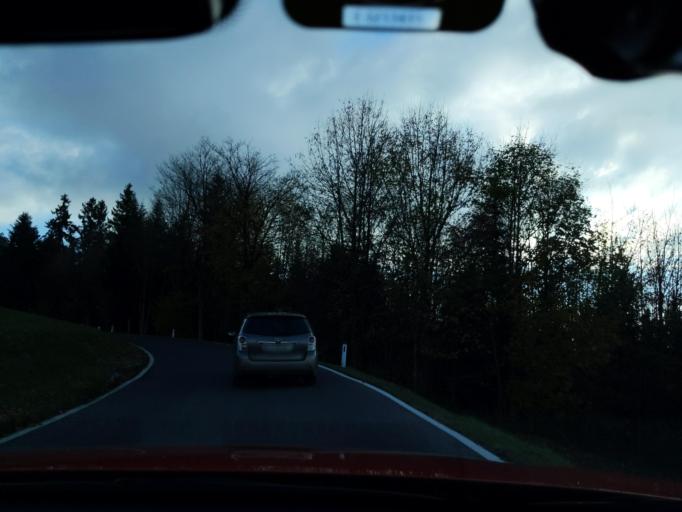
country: AT
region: Vorarlberg
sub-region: Politischer Bezirk Bregenz
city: Eichenberg
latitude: 47.5582
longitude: 9.7884
